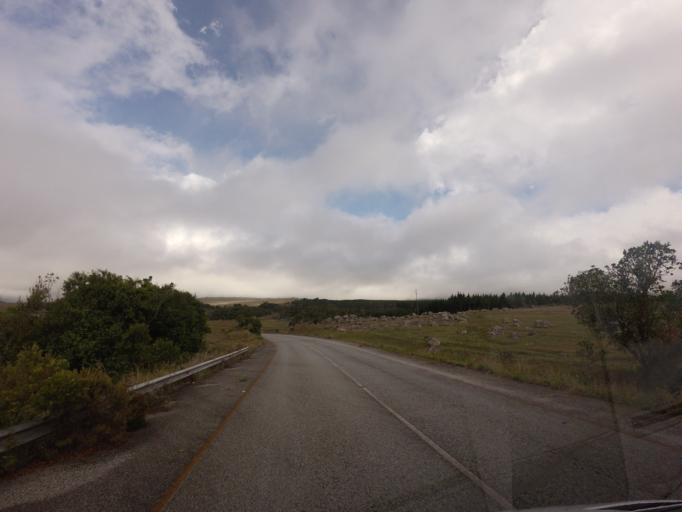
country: ZA
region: Mpumalanga
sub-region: Ehlanzeni District
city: Graksop
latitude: -24.8564
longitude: 30.8806
